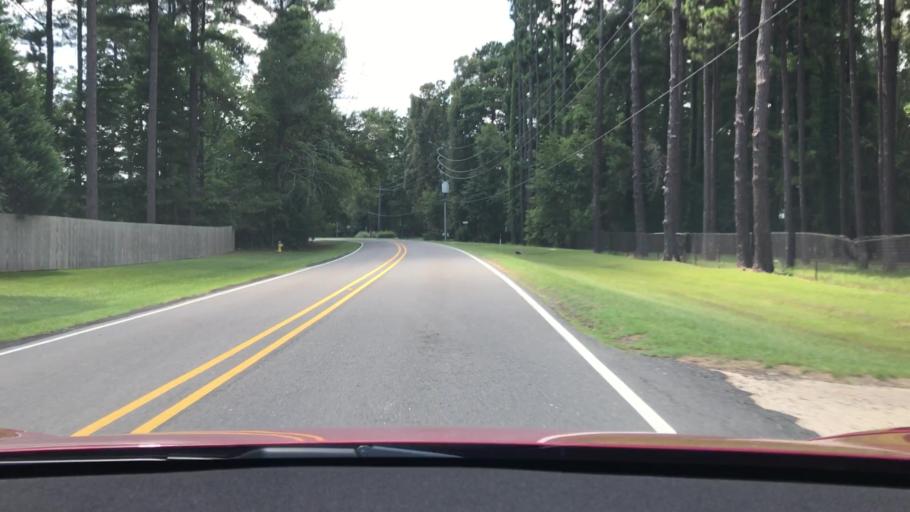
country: US
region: Louisiana
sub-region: De Soto Parish
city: Stonewall
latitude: 32.3691
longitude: -93.7039
